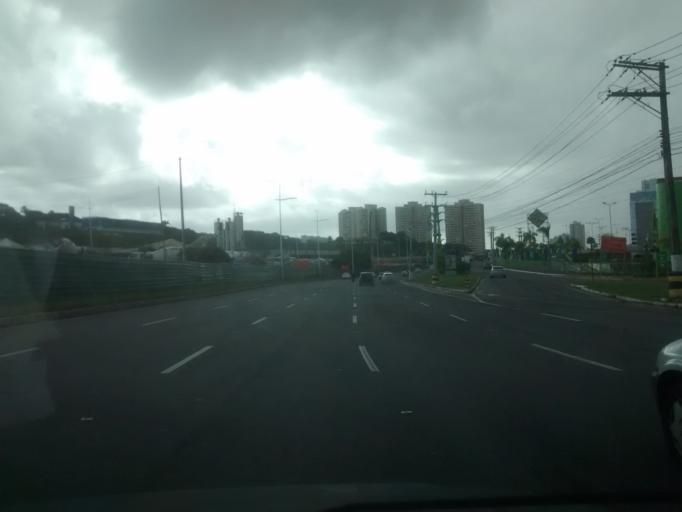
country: BR
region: Bahia
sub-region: Salvador
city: Salvador
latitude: -12.9418
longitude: -38.4184
